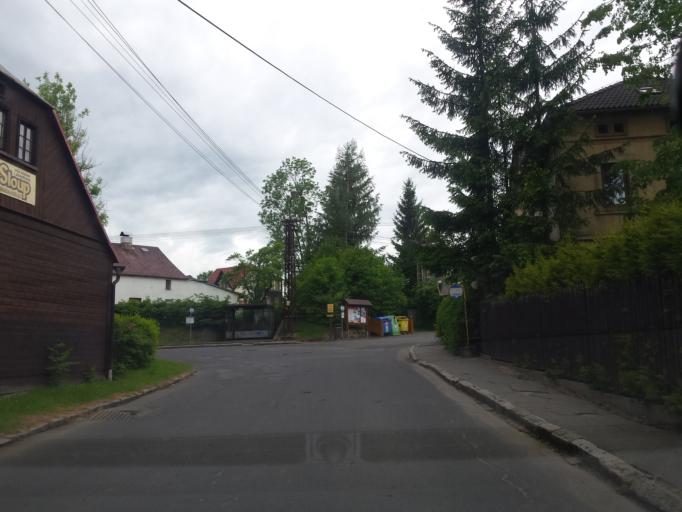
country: CZ
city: Novy Bor
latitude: 50.7446
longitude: 14.5915
